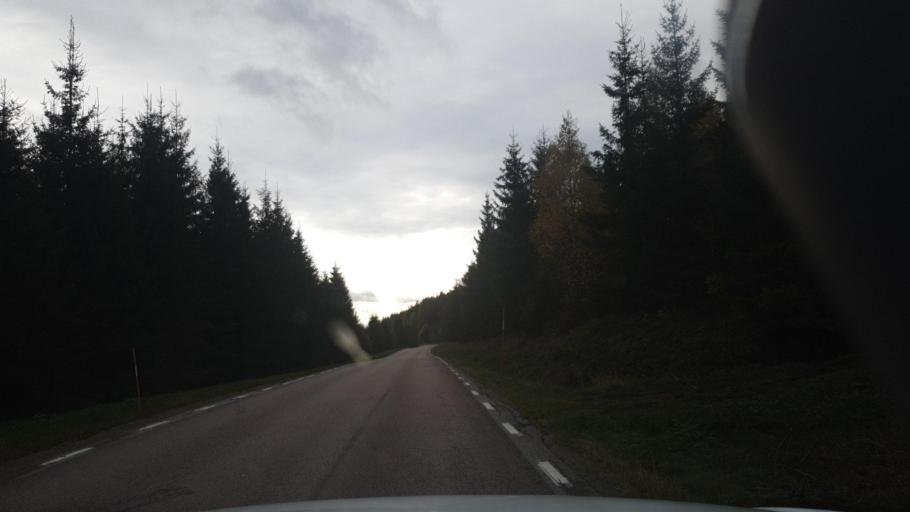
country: SE
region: Vaermland
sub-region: Arvika Kommun
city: Arvika
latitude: 59.7076
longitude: 12.7919
